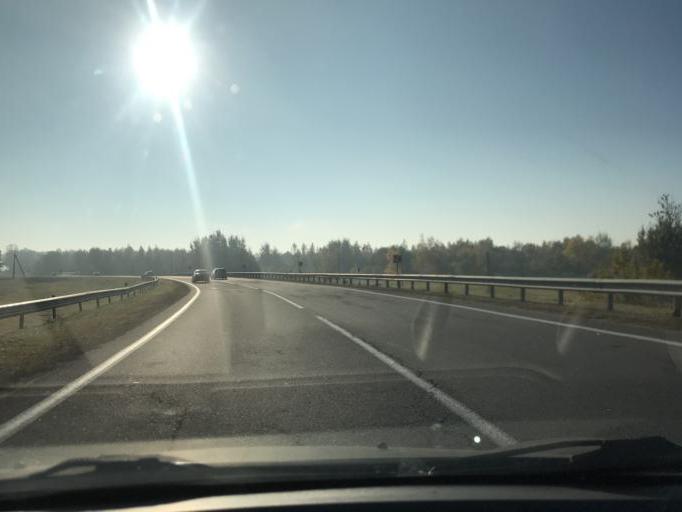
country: BY
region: Minsk
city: Dukora
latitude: 53.6630
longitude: 27.9402
